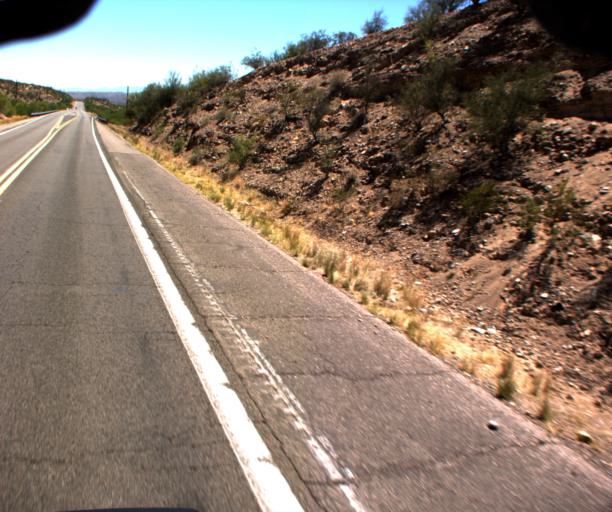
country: US
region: Arizona
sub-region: Pinal County
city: Mammoth
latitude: 32.9046
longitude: -110.7177
